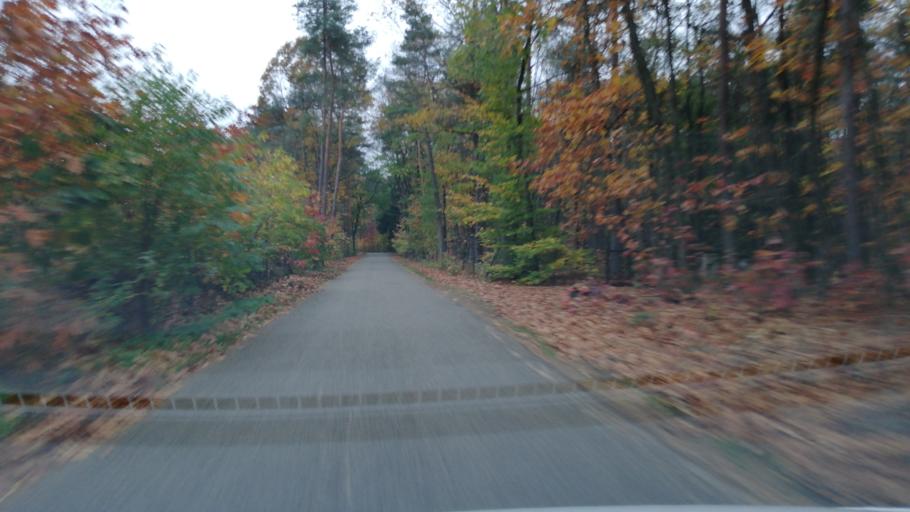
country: NL
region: Gelderland
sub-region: Gemeente Apeldoorn
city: Beekbergen
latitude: 52.1377
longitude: 5.9659
